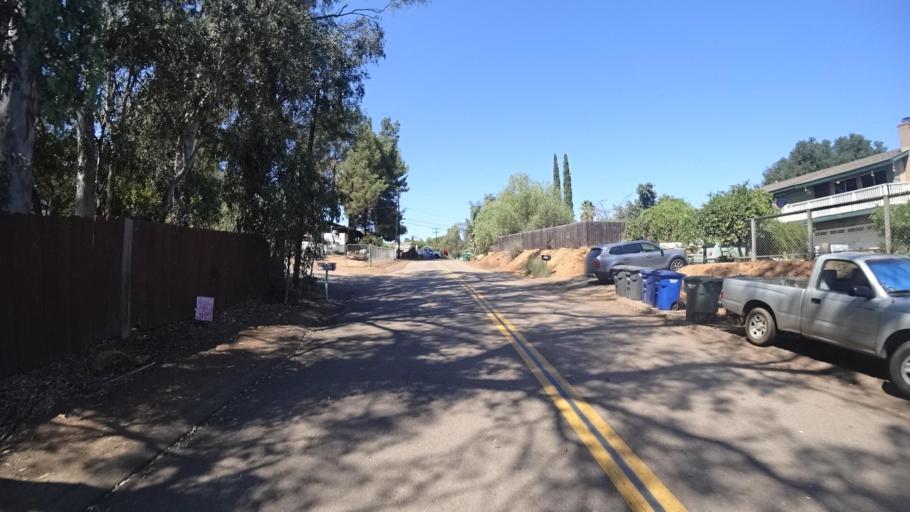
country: US
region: California
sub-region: San Diego County
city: Crest
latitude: 32.8017
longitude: -116.8681
